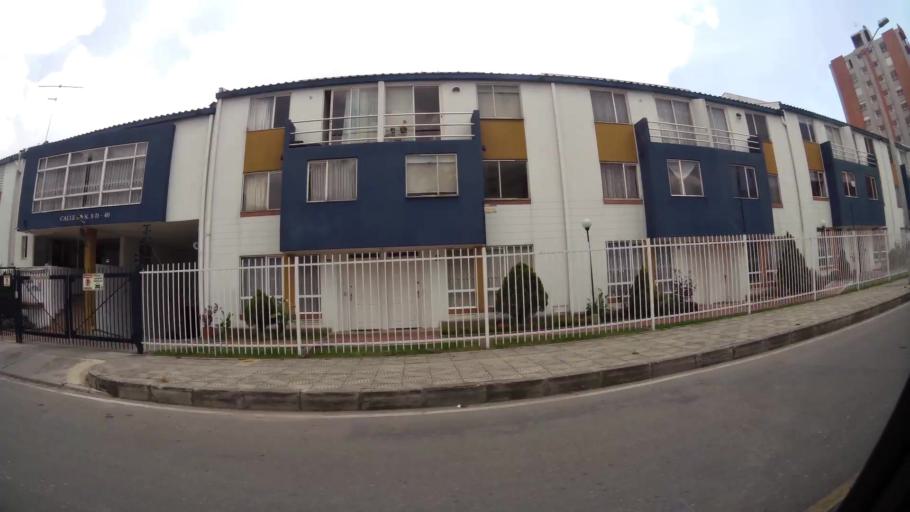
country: CO
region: Cundinamarca
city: La Calera
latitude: 4.7457
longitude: -74.0279
